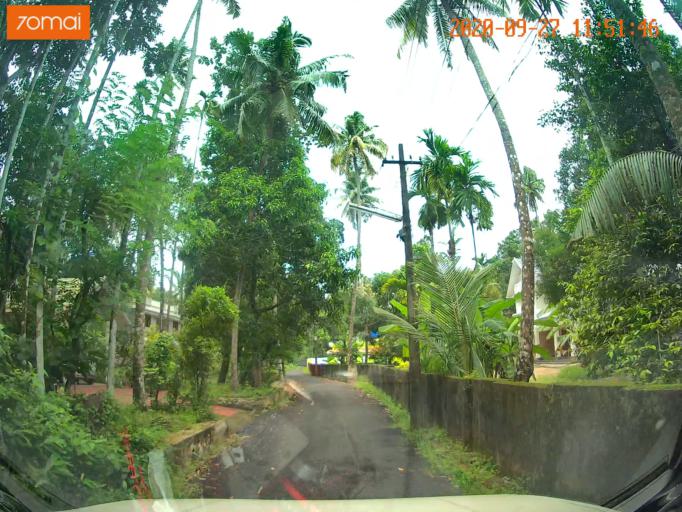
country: IN
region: Kerala
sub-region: Thrissur District
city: Thanniyam
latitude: 10.4726
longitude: 76.1172
